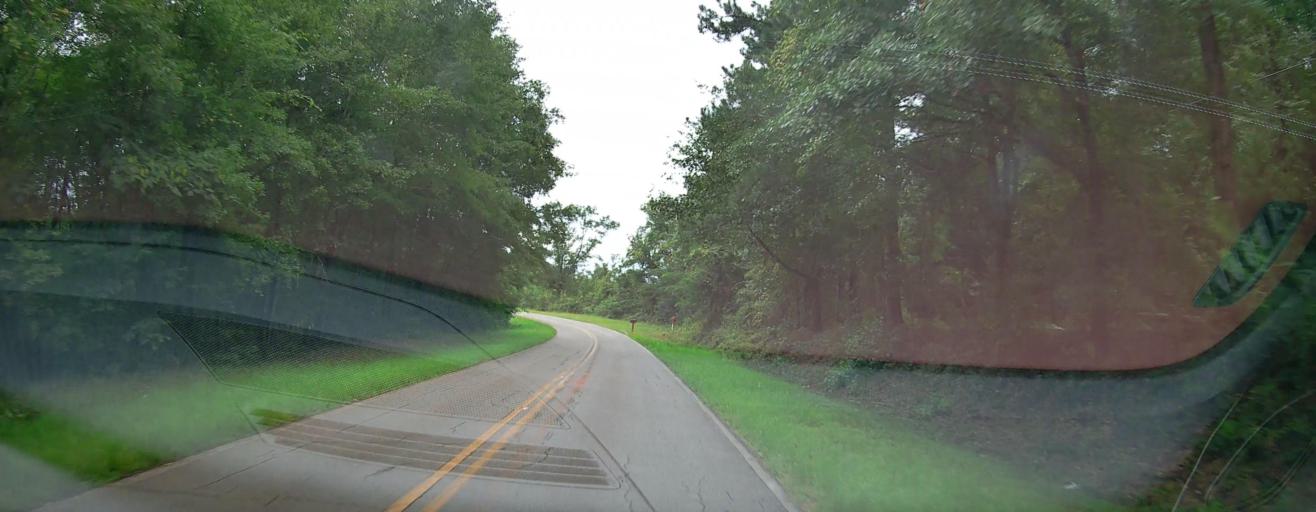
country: US
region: Georgia
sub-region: Bibb County
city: Macon
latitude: 32.7778
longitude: -83.5135
